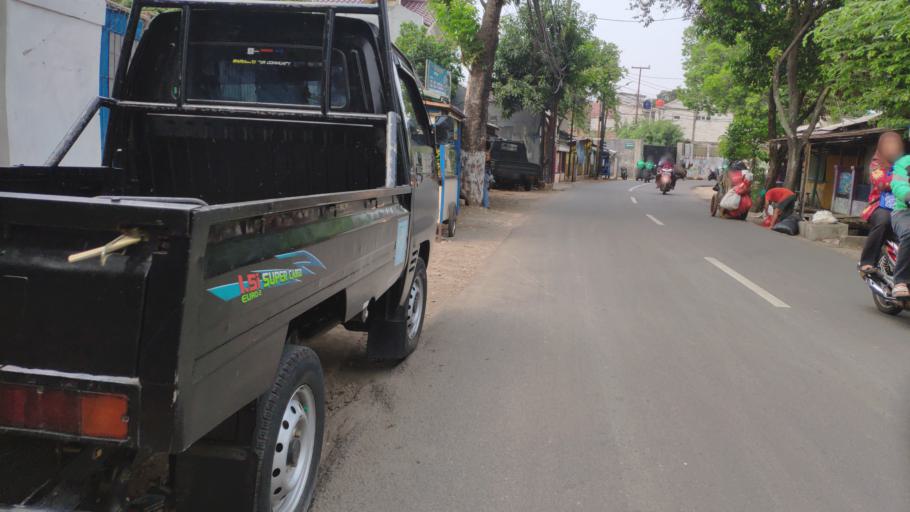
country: ID
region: West Java
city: Depok
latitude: -6.3450
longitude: 106.8118
